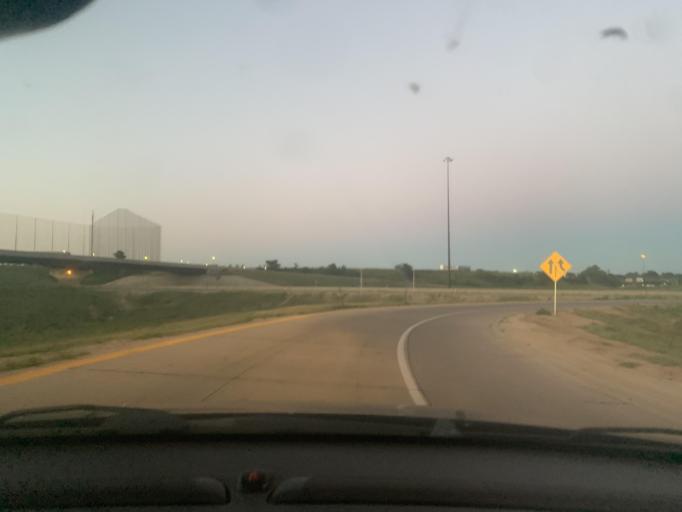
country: US
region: Nebraska
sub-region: Douglas County
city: Ralston
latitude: 41.2647
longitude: -96.0775
